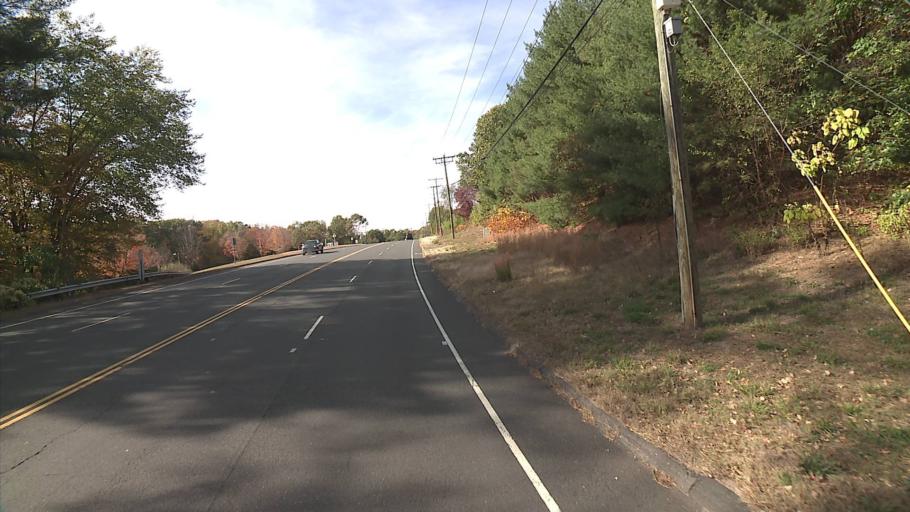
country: US
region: Connecticut
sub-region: Hartford County
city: Plainville
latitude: 41.7051
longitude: -72.8673
